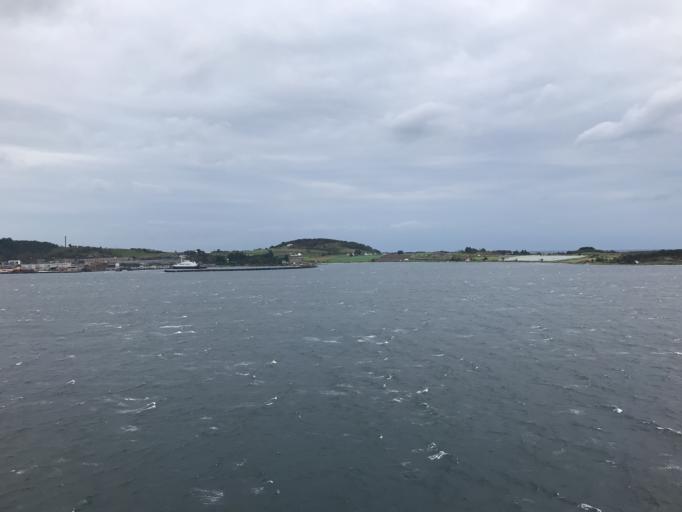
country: NO
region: Rogaland
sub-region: Randaberg
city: Randaberg
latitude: 59.0340
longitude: 5.6200
